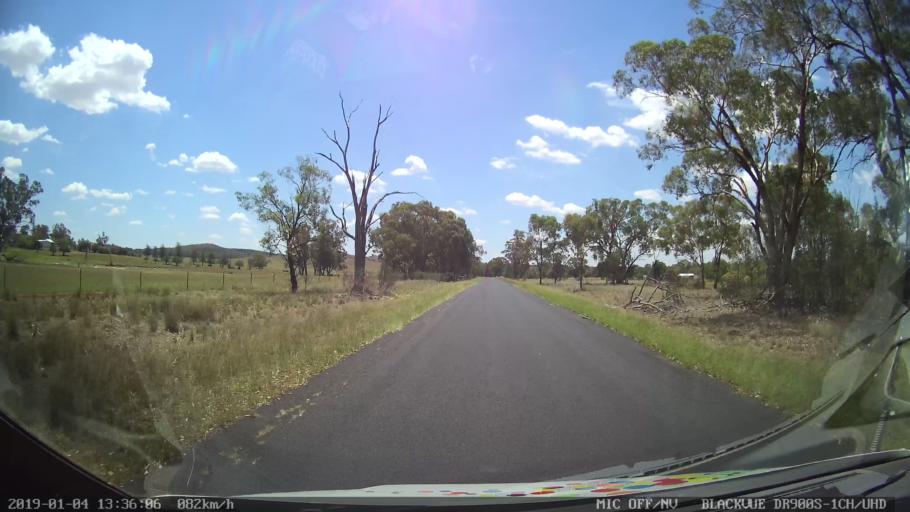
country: AU
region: New South Wales
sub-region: Dubbo Municipality
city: Dubbo
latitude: -32.5650
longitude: 148.5365
